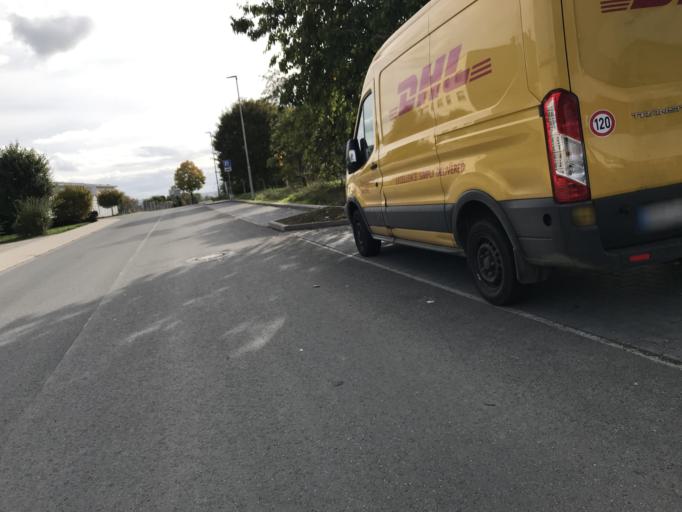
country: DE
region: Hesse
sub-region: Regierungsbezirk Darmstadt
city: Butzbach
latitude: 50.4271
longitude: 8.6660
